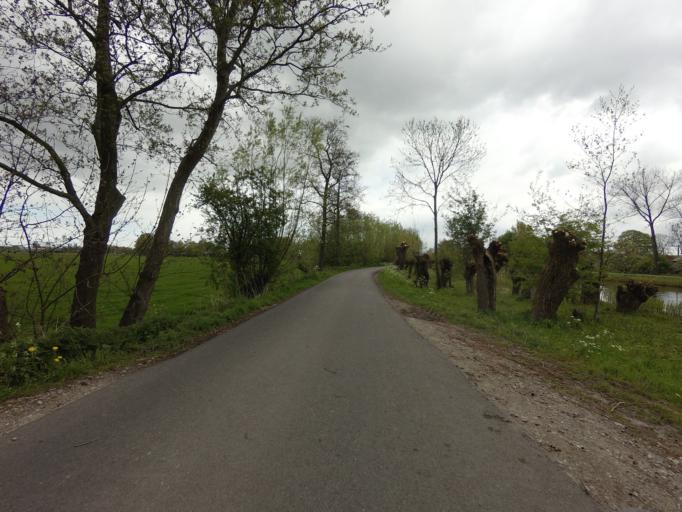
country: NL
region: North Holland
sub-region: Gemeente Amsterdam
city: Driemond
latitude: 52.2792
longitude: 5.0011
